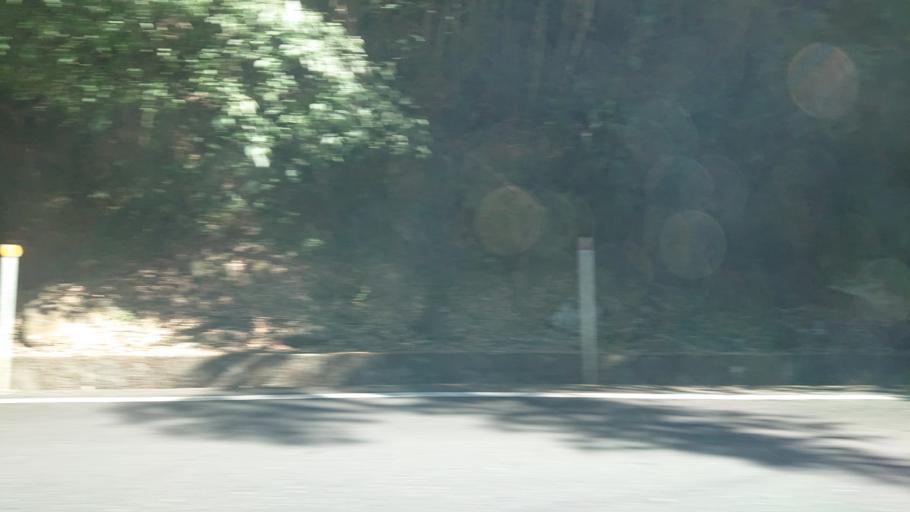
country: TW
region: Taiwan
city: Lugu
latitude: 23.4807
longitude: 120.7433
